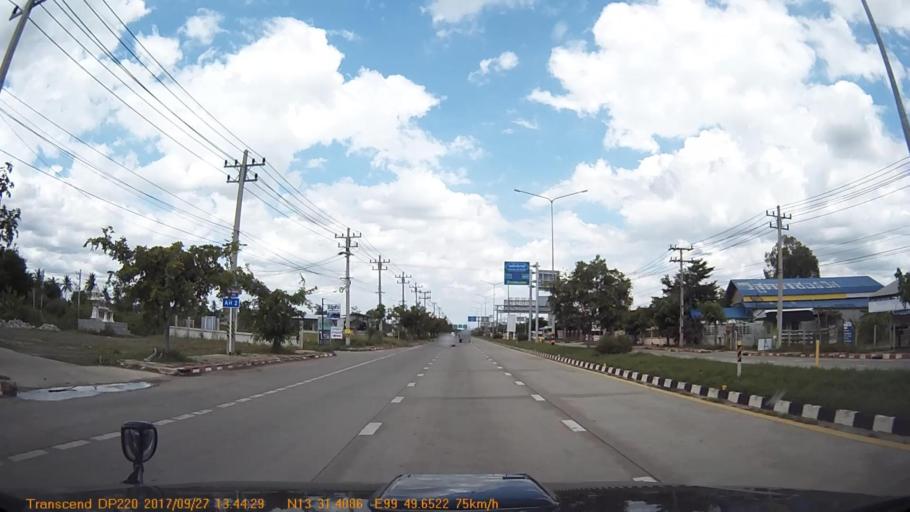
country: TH
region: Ratchaburi
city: Ratchaburi
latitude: 13.5234
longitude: 99.8275
